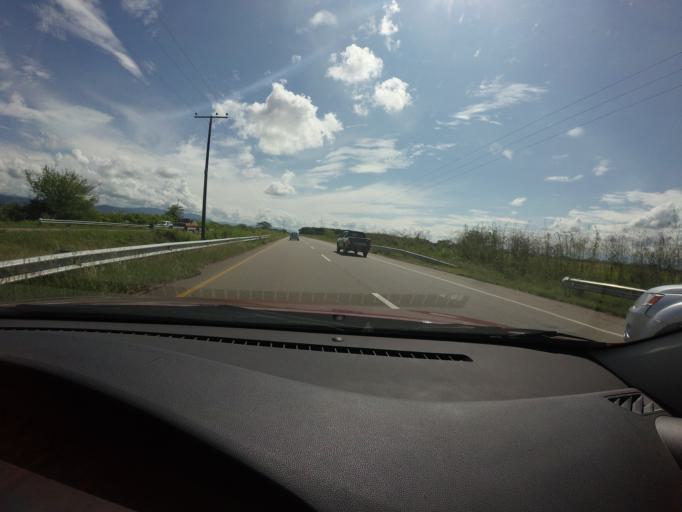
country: CO
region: Antioquia
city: Puerto Triunfo
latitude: 5.6835
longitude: -74.6117
